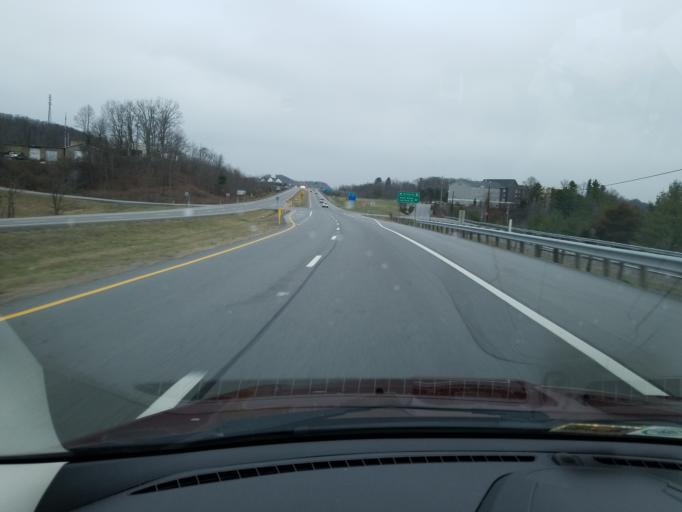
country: US
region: West Virginia
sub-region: Mercer County
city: Athens
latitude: 37.3646
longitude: -81.0359
